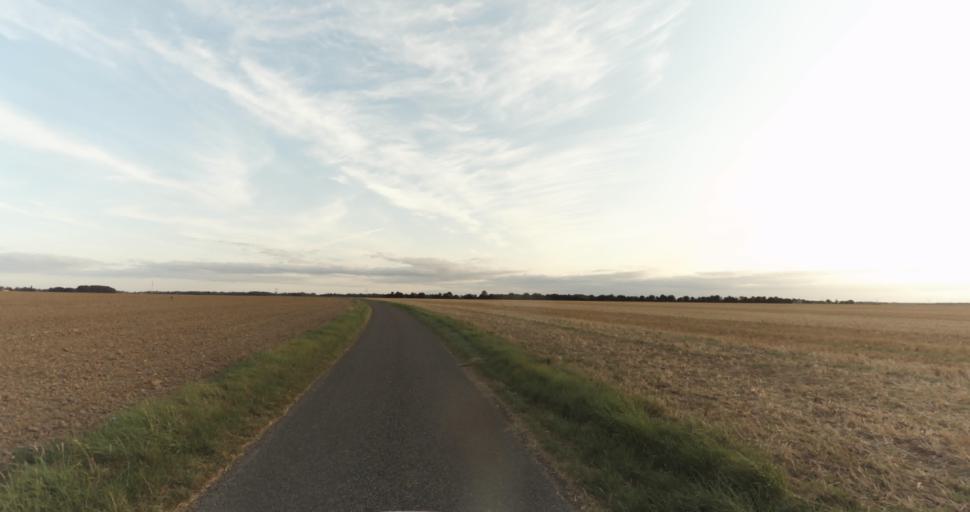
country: FR
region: Haute-Normandie
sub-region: Departement de l'Eure
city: La Madeleine-de-Nonancourt
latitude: 48.8762
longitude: 1.2321
